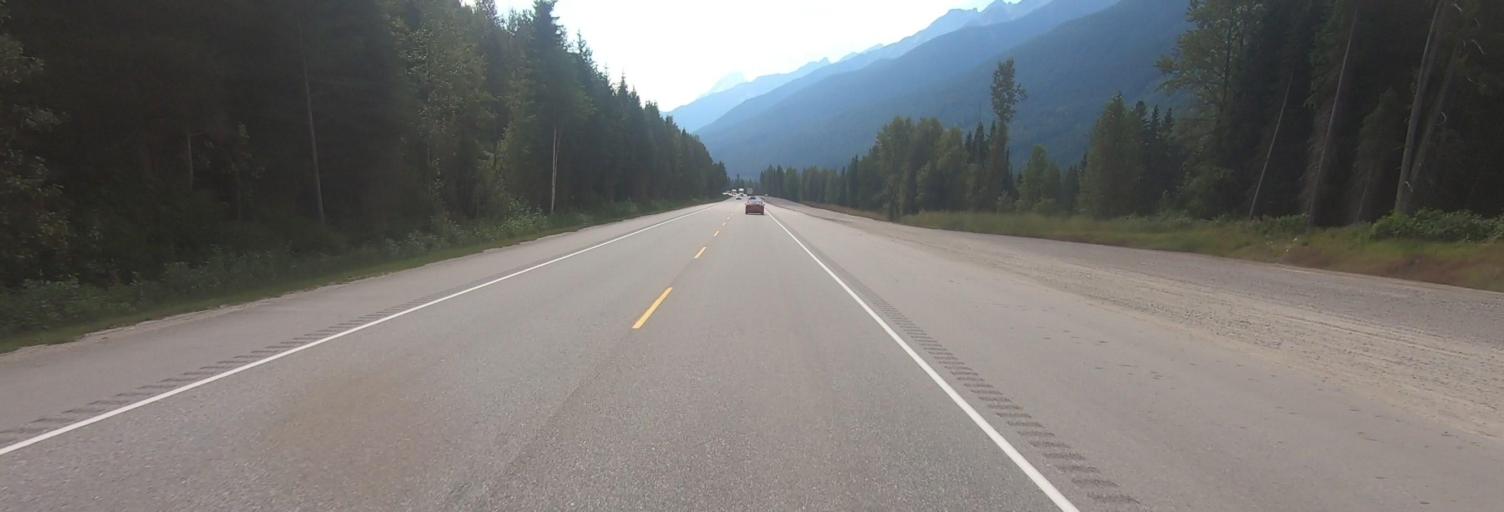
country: CA
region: British Columbia
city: Golden
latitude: 51.4136
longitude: -117.4723
